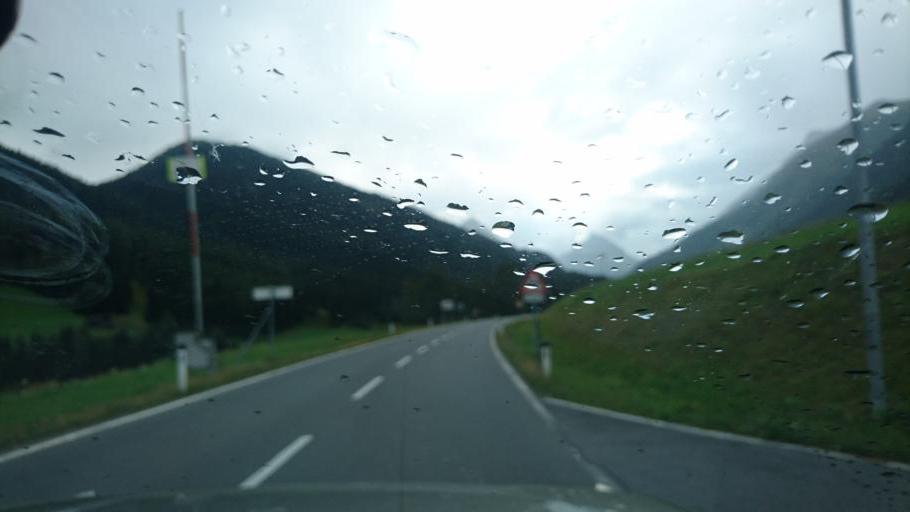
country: AT
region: Tyrol
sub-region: Politischer Bezirk Landeck
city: Ischgl
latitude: 46.9893
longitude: 10.2405
